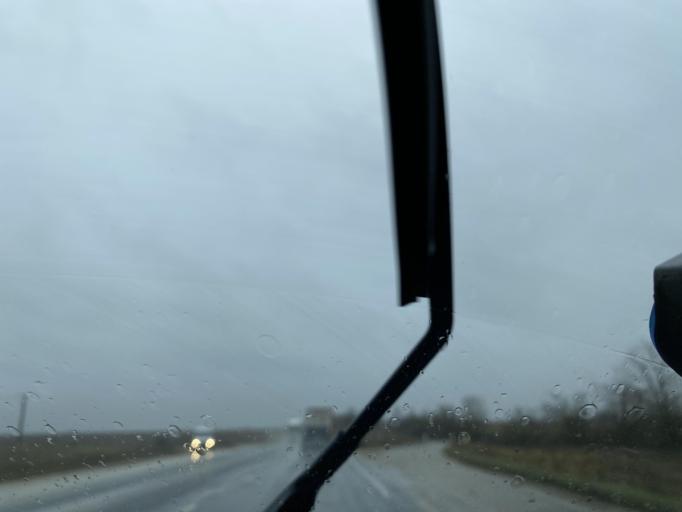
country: FR
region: Centre
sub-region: Departement d'Eure-et-Loir
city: Voves
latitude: 48.2841
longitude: 1.7267
